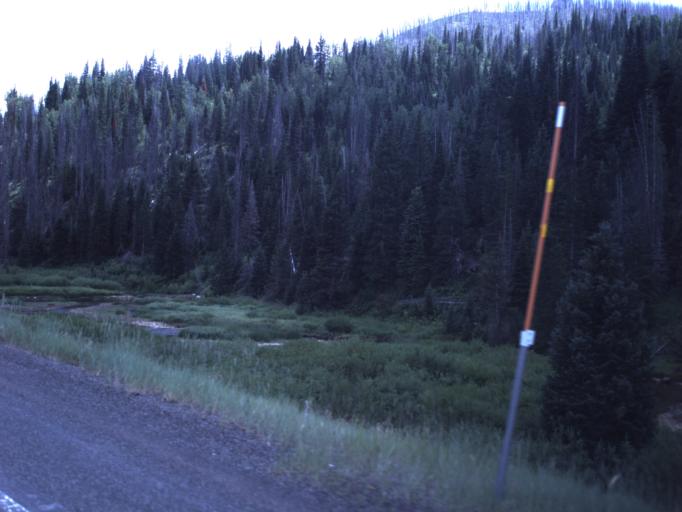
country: US
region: Utah
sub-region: Sanpete County
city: Fairview
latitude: 39.5933
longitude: -111.2036
